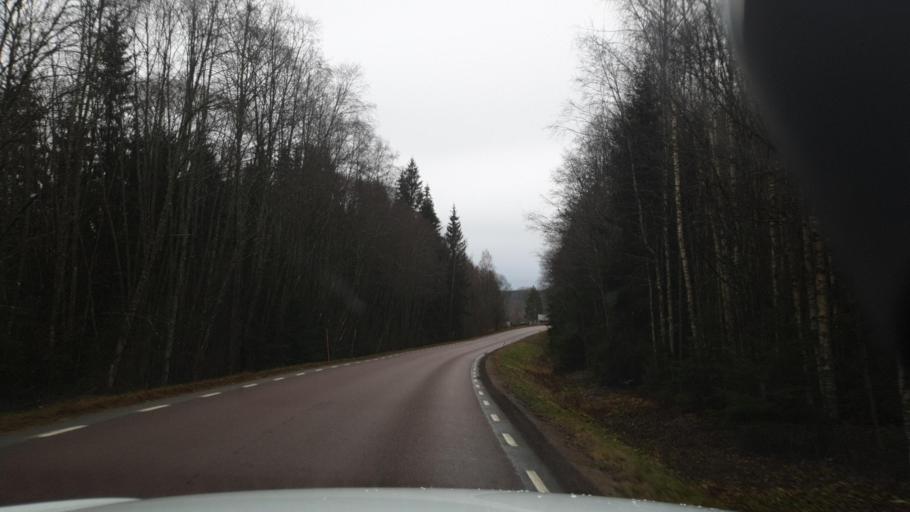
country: SE
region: Vaermland
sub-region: Arvika Kommun
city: Arvika
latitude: 59.6925
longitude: 12.7914
